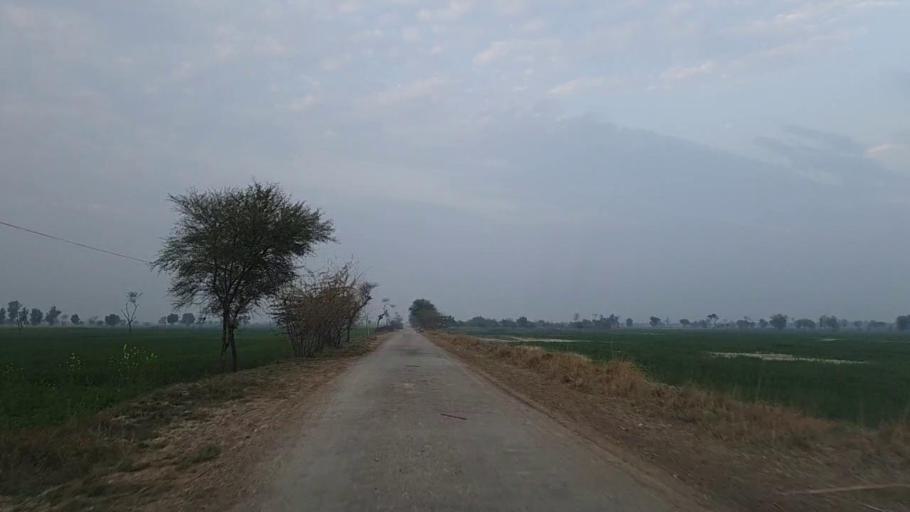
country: PK
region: Sindh
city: Jam Sahib
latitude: 26.3025
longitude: 68.5936
